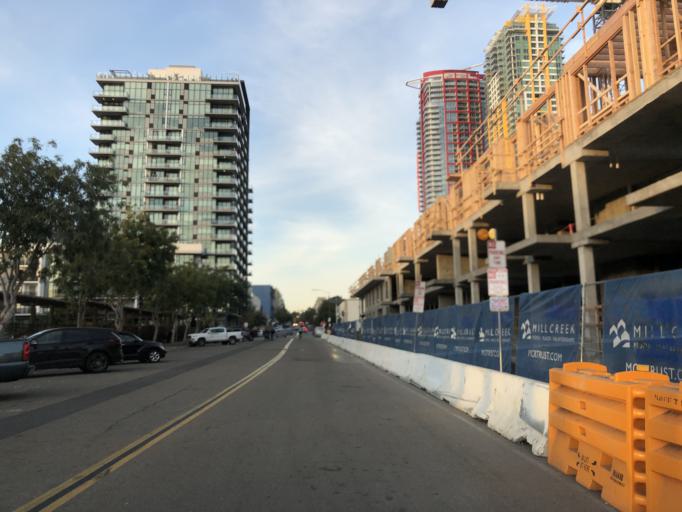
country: US
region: California
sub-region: San Diego County
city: San Diego
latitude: 32.7074
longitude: -117.1519
